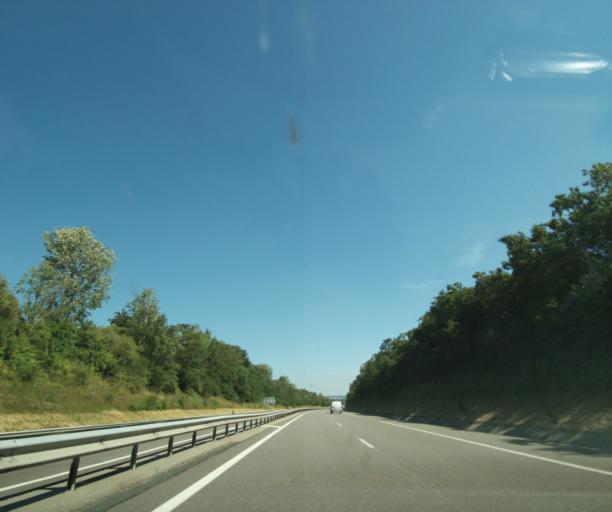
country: FR
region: Lorraine
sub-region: Departement des Vosges
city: Chatenois
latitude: 48.2805
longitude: 5.8557
